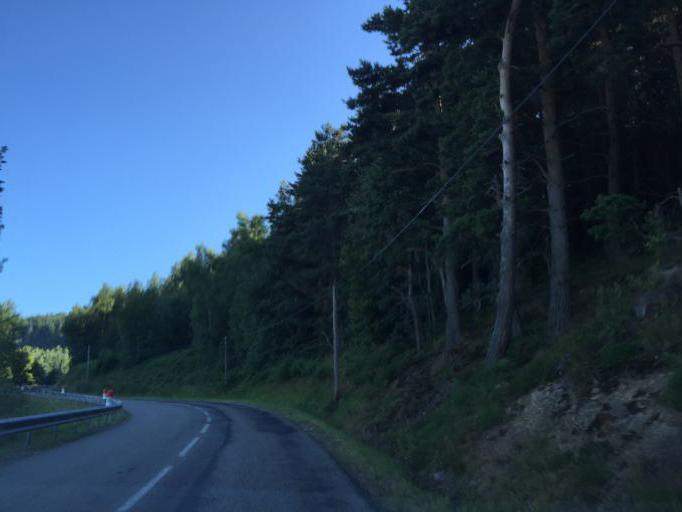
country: FR
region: Rhone-Alpes
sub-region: Departement de la Loire
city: Saint-Chamond
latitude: 45.4011
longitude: 4.5330
